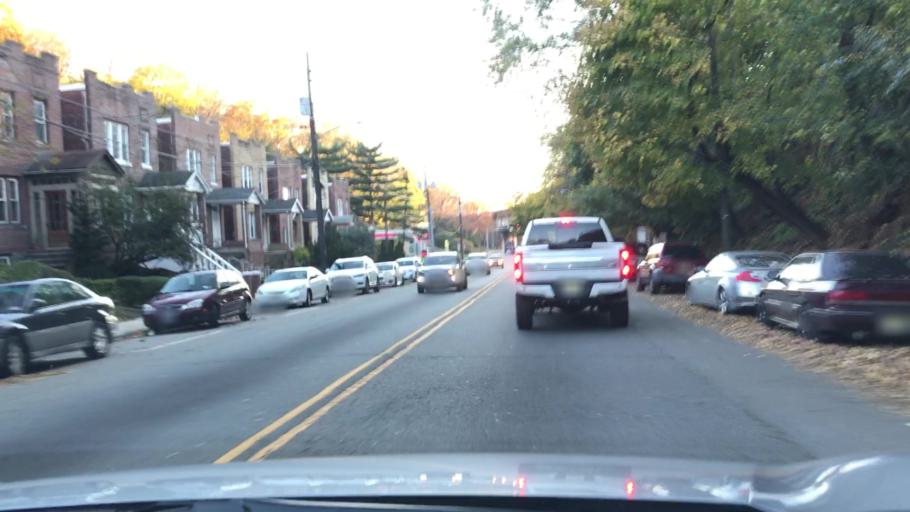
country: US
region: New Jersey
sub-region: Hudson County
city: Weehawken
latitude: 40.7699
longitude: -74.0210
